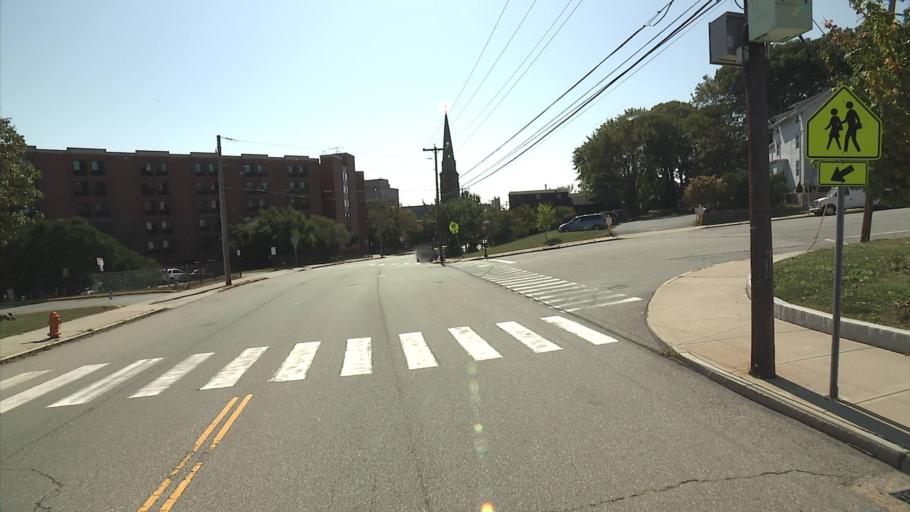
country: US
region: Connecticut
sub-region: New London County
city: New London
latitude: 41.3586
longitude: -72.0994
